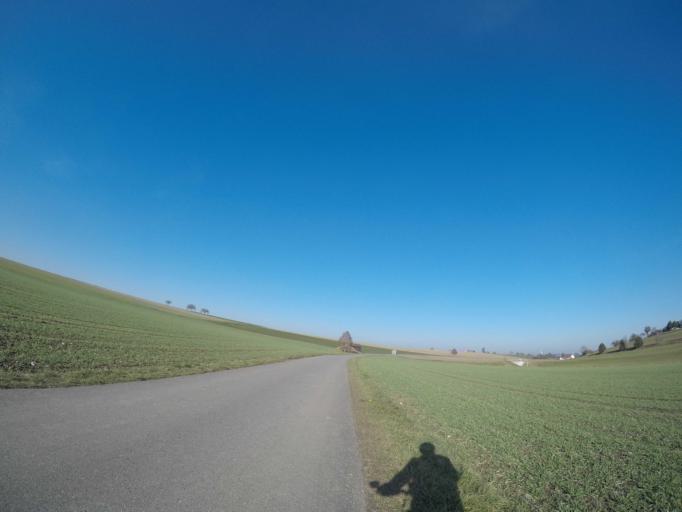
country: DE
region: Baden-Wuerttemberg
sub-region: Tuebingen Region
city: Unterwachingen
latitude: 48.2106
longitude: 9.6462
